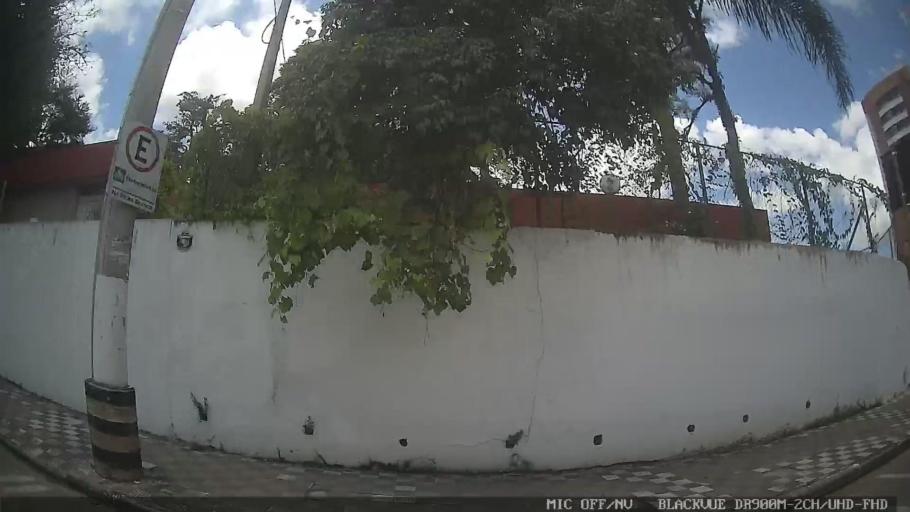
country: BR
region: Sao Paulo
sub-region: Jacarei
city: Jacarei
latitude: -23.3017
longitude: -45.9589
